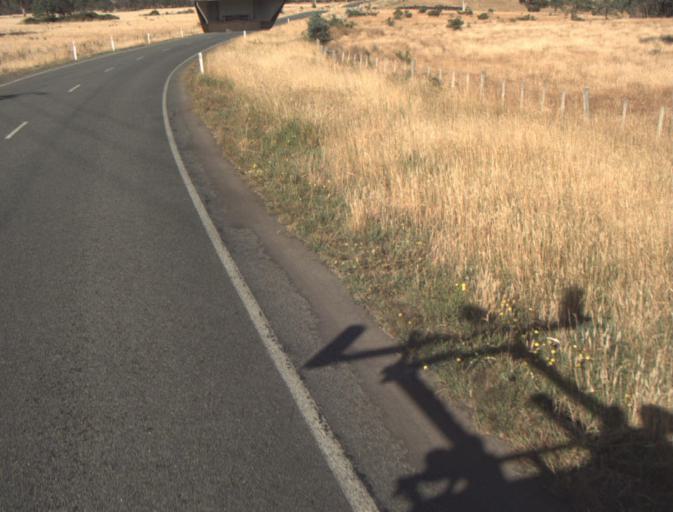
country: AU
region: Tasmania
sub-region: Launceston
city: Newstead
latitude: -41.4455
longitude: 147.2514
